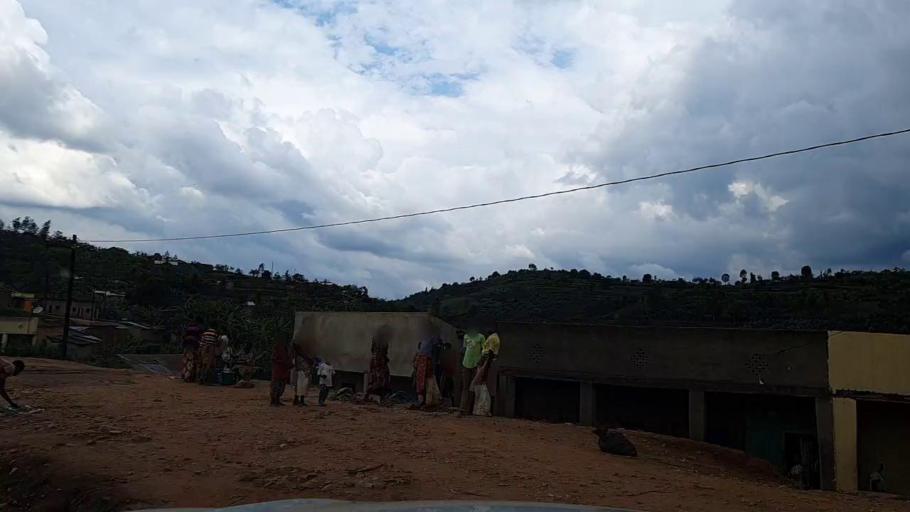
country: RW
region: Southern Province
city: Gikongoro
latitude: -2.4176
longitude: 29.6636
